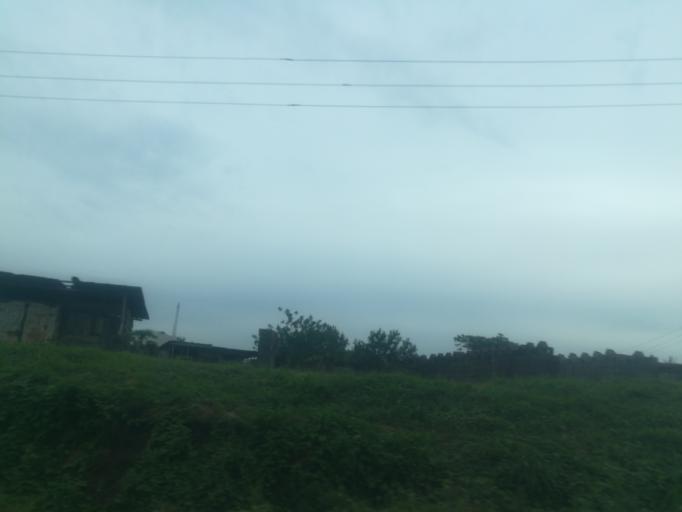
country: NG
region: Oyo
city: Egbeda
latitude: 7.3828
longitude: 4.0157
